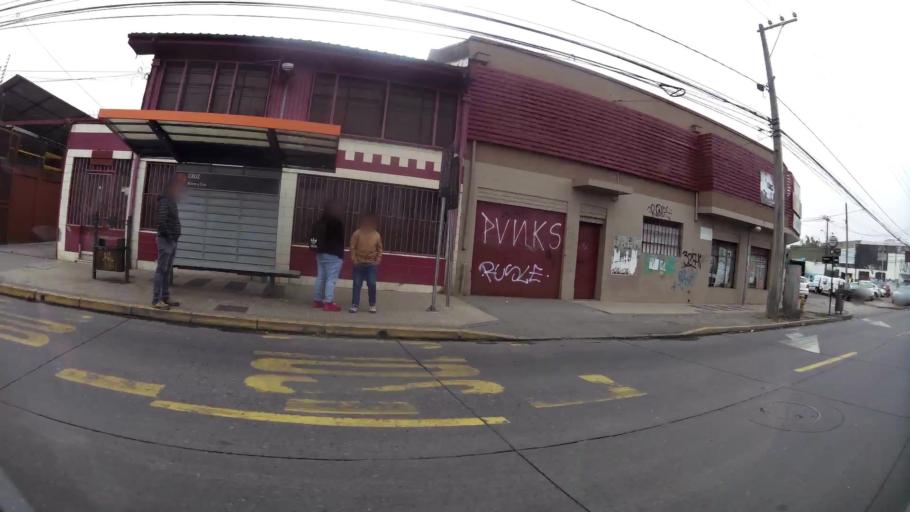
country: CL
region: Biobio
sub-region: Provincia de Concepcion
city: Concepcion
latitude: -36.8233
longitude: -73.0630
